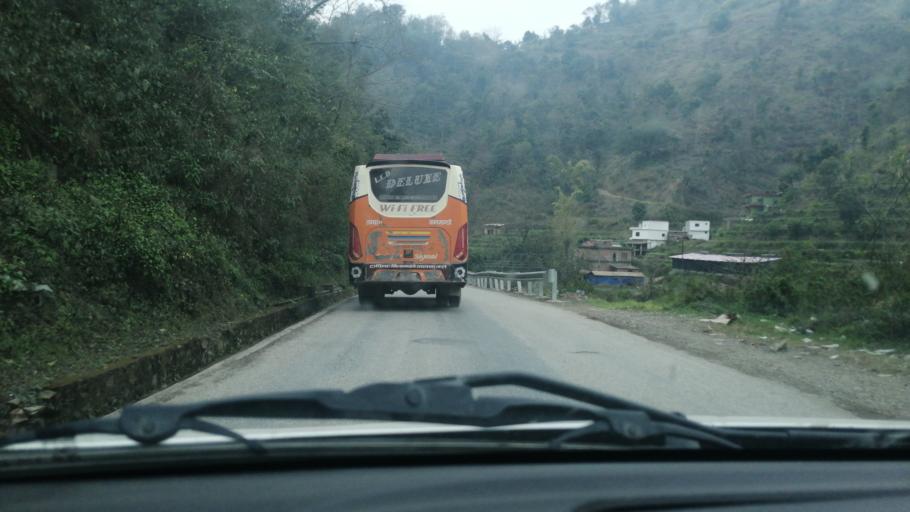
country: NP
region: Western Region
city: Tansen
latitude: 27.8085
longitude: 83.5153
